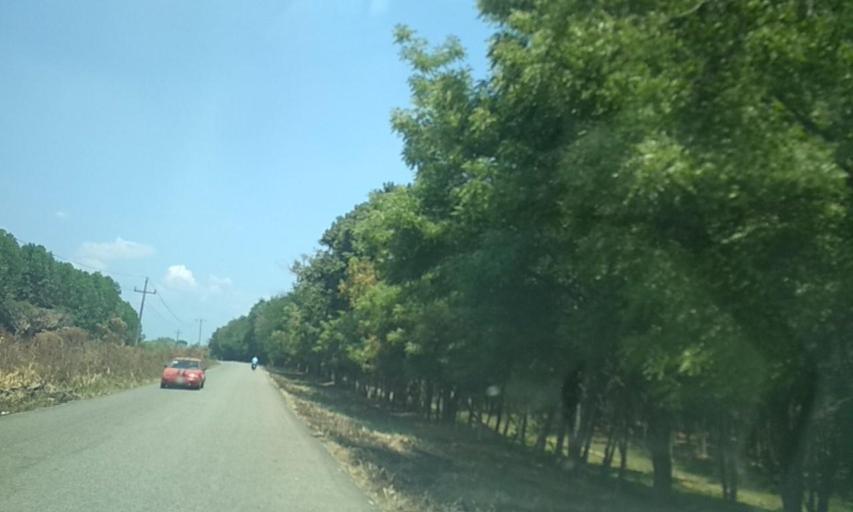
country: MX
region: Tabasco
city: Huimanguillo
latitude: 17.7998
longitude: -93.4686
